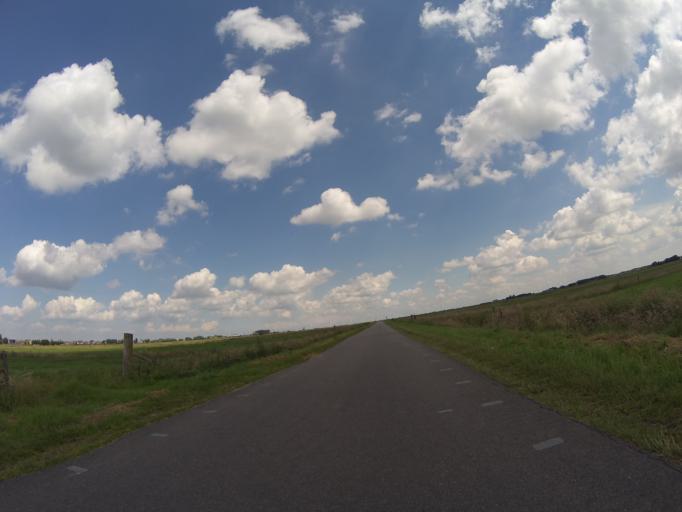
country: NL
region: Utrecht
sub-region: Gemeente Bunschoten
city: Spakenburg
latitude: 52.2482
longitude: 5.3371
